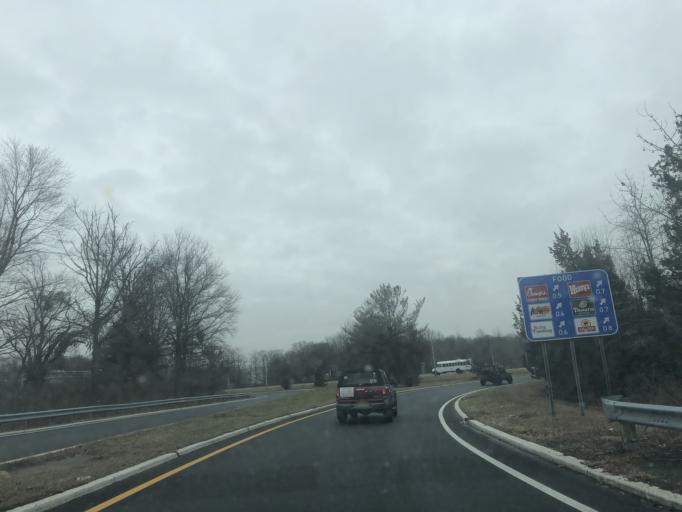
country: US
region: New Jersey
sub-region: Mercer County
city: Robbinsville
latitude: 40.2039
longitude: -74.6359
